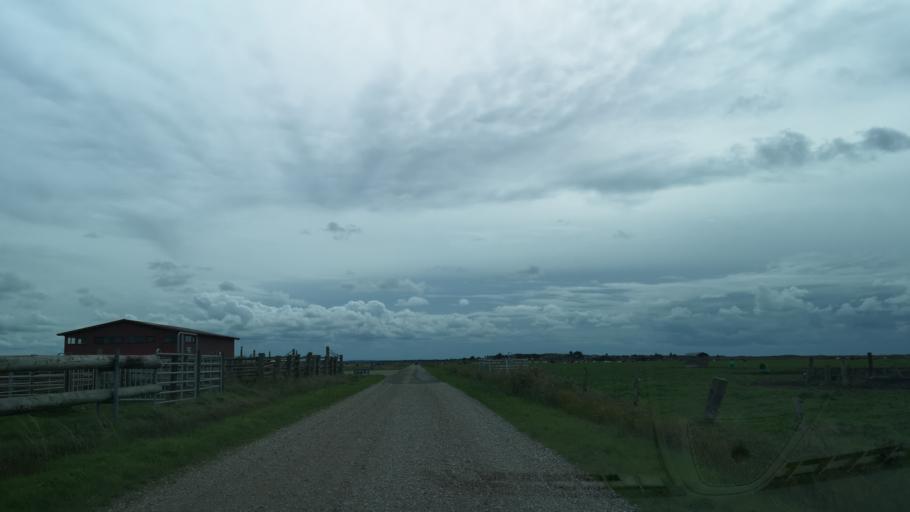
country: DK
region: Central Jutland
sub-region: Ringkobing-Skjern Kommune
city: Hvide Sande
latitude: 55.8625
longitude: 8.2202
